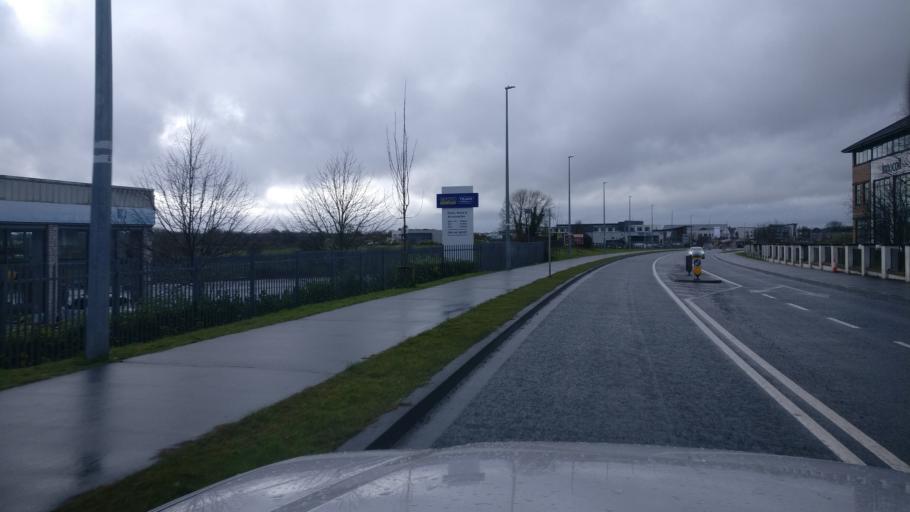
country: IE
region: Leinster
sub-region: An Iarmhi
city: Athlone
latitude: 53.4207
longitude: -7.9909
